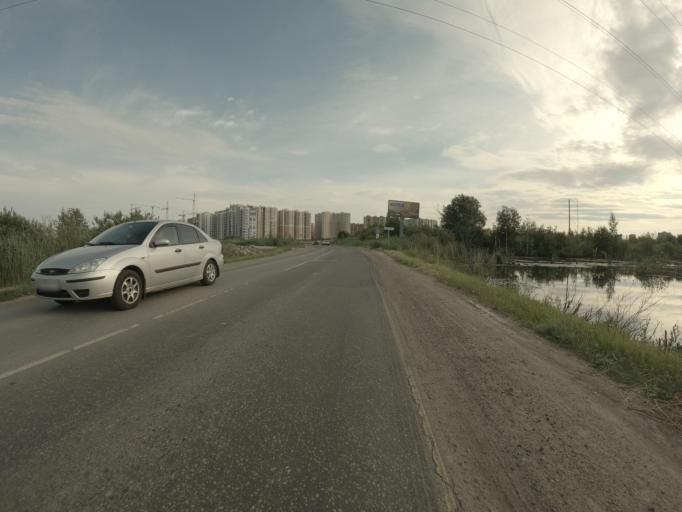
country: RU
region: St.-Petersburg
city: Krasnogvargeisky
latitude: 59.9249
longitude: 30.5185
